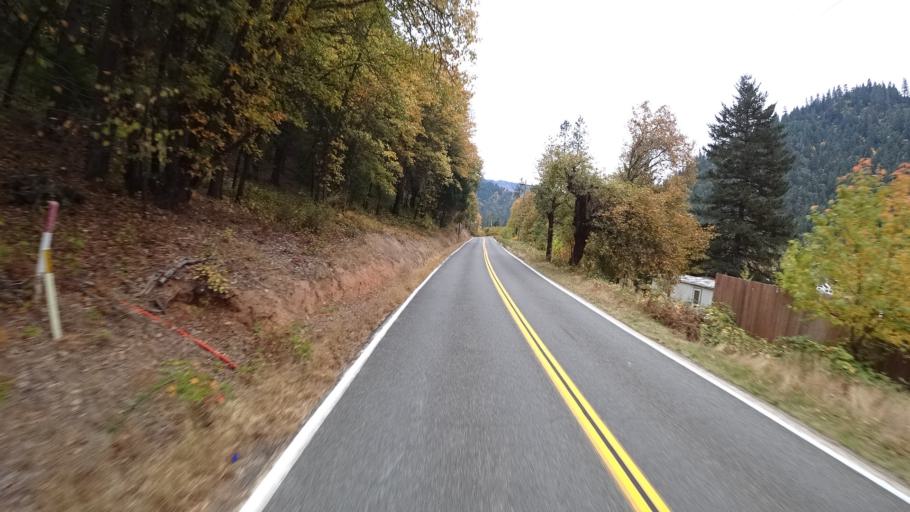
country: US
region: California
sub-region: Siskiyou County
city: Happy Camp
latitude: 41.8582
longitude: -123.3946
